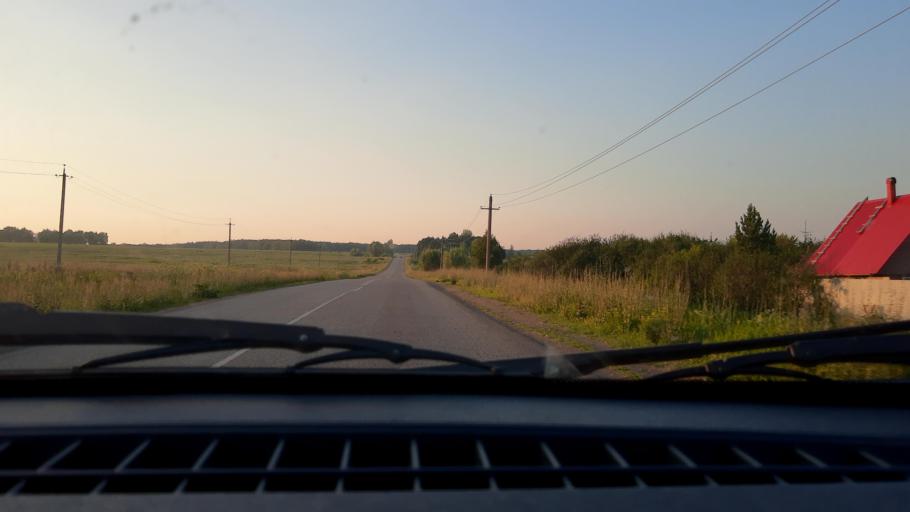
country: RU
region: Bashkortostan
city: Mikhaylovka
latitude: 54.9167
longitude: 55.8775
